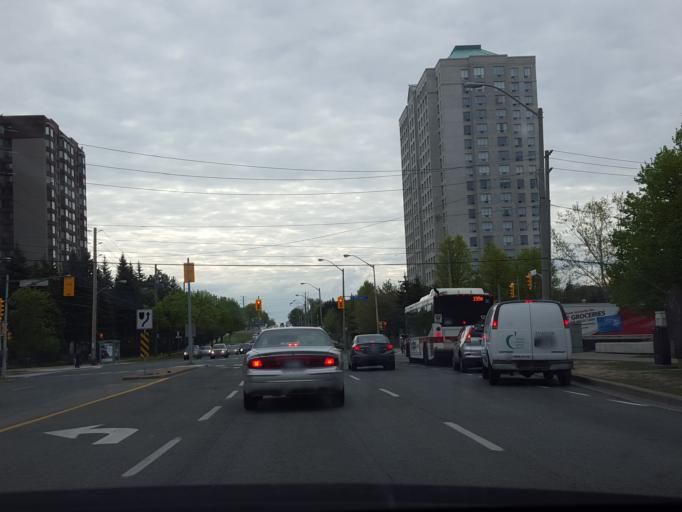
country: CA
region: Ontario
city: Scarborough
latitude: 43.8078
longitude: -79.2675
